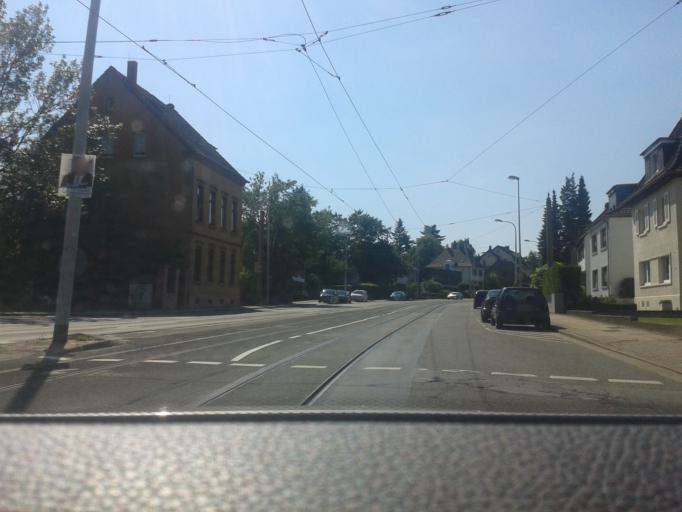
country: DE
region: North Rhine-Westphalia
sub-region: Regierungsbezirk Dusseldorf
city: Muelheim (Ruhr)
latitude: 51.4138
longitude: 6.8585
